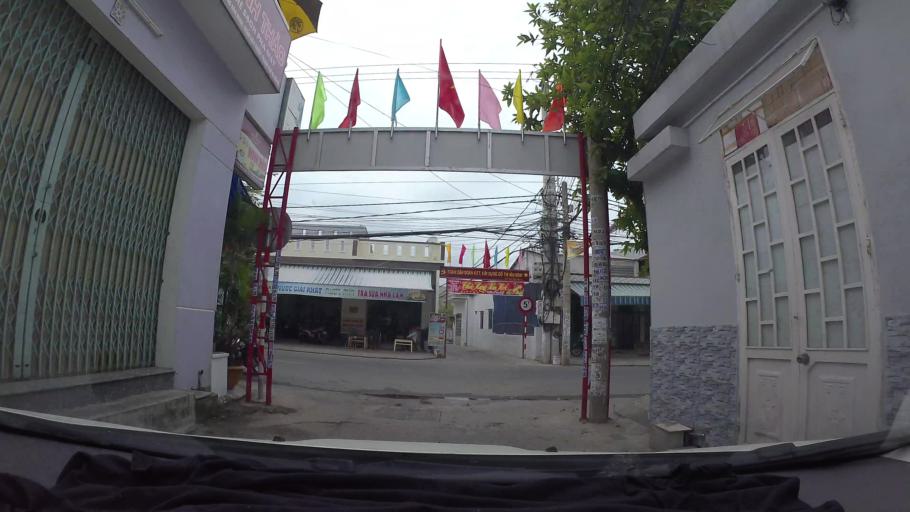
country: VN
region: Da Nang
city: Lien Chieu
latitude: 16.0642
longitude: 108.1669
